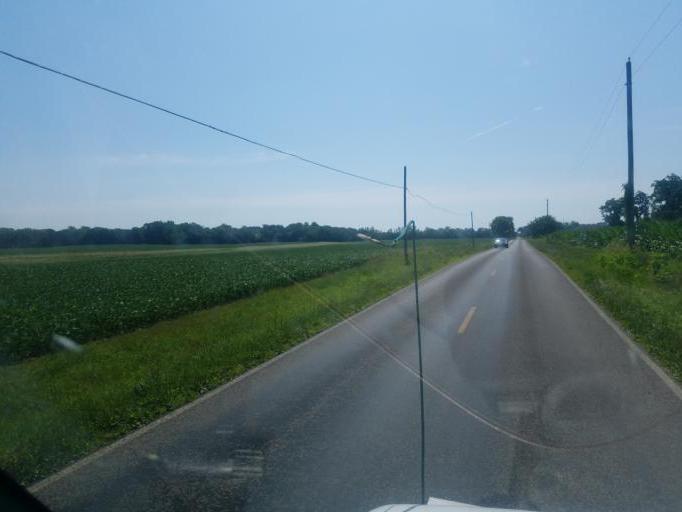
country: US
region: Ohio
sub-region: Champaign County
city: North Lewisburg
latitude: 40.2157
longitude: -83.5081
